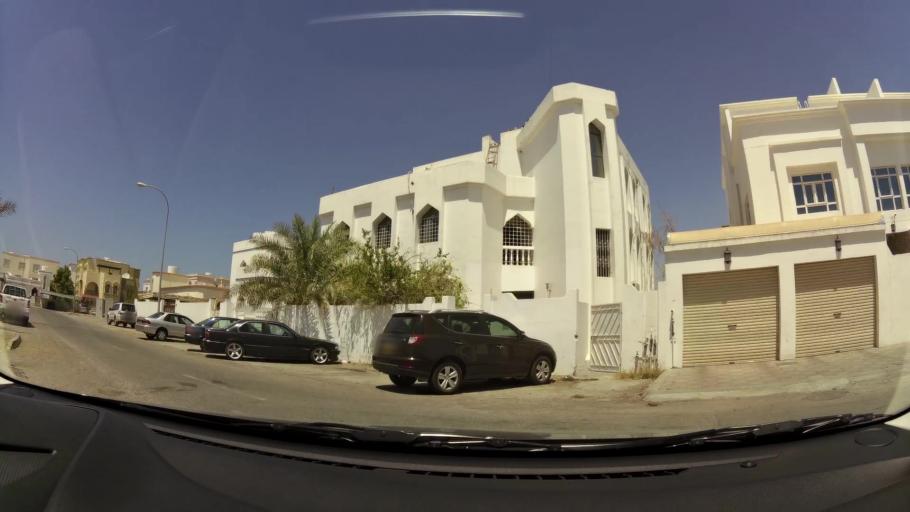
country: OM
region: Muhafazat Masqat
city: Bawshar
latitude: 23.5972
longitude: 58.3778
